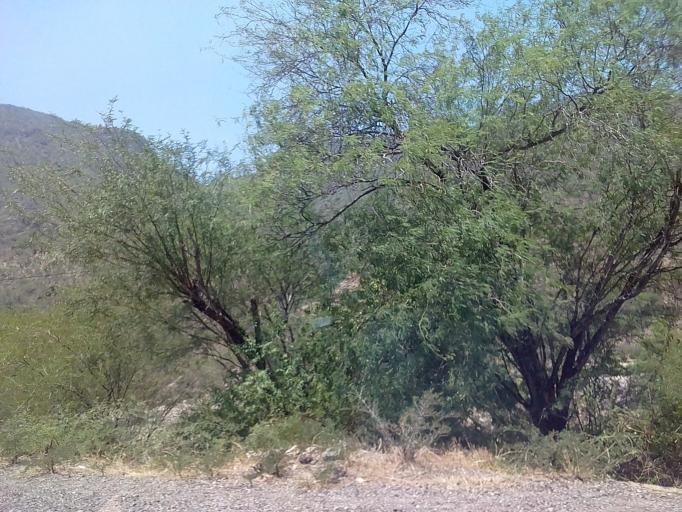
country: MX
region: Oaxaca
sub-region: San Pedro Quiatoni
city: San Pedro Quiatoni
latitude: 16.6686
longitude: -96.1407
